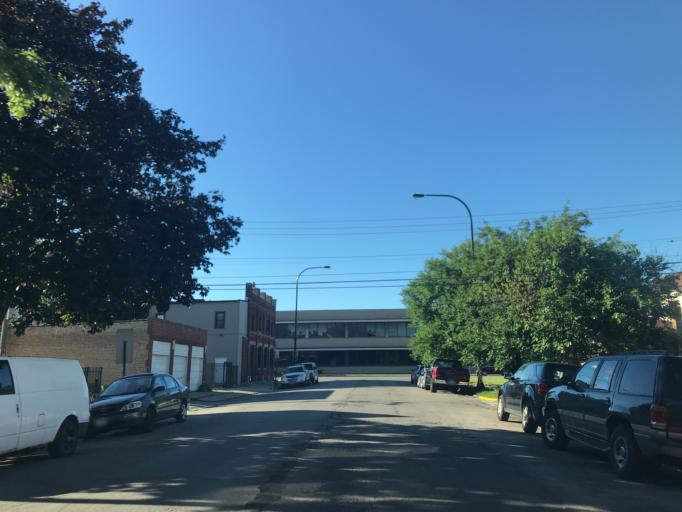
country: US
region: Illinois
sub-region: Cook County
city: Cicero
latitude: 41.8647
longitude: -87.7496
